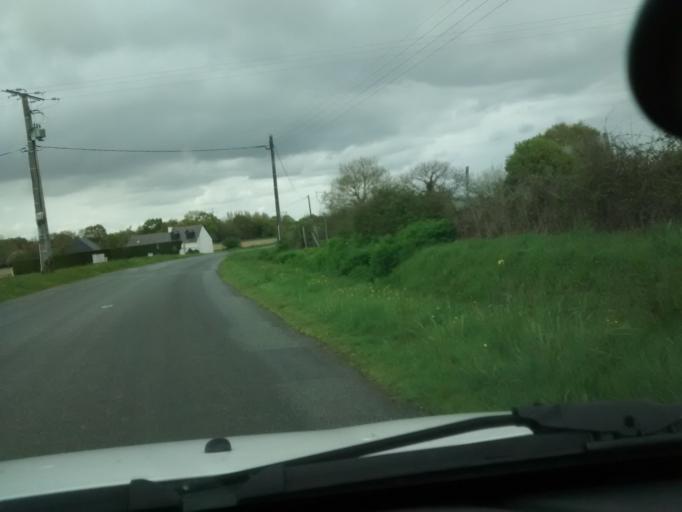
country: FR
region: Brittany
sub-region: Departement d'Ille-et-Vilaine
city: Nouvoitou
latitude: 48.0752
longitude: -1.5466
